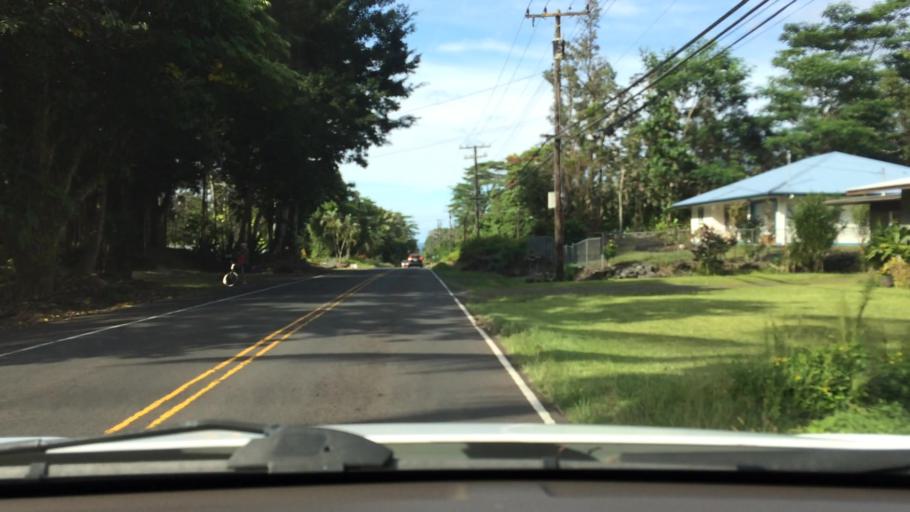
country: US
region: Hawaii
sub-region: Hawaii County
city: Hawaiian Beaches
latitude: 19.5443
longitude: -154.9047
